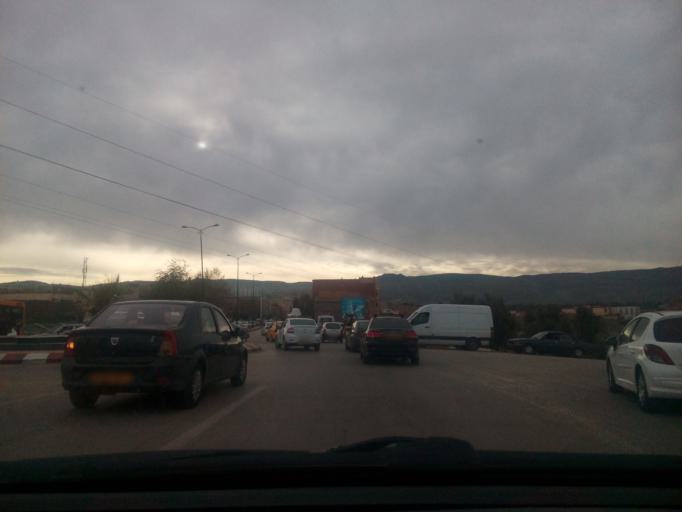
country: DZ
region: Tlemcen
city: Mansoura
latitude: 34.8848
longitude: -1.3523
